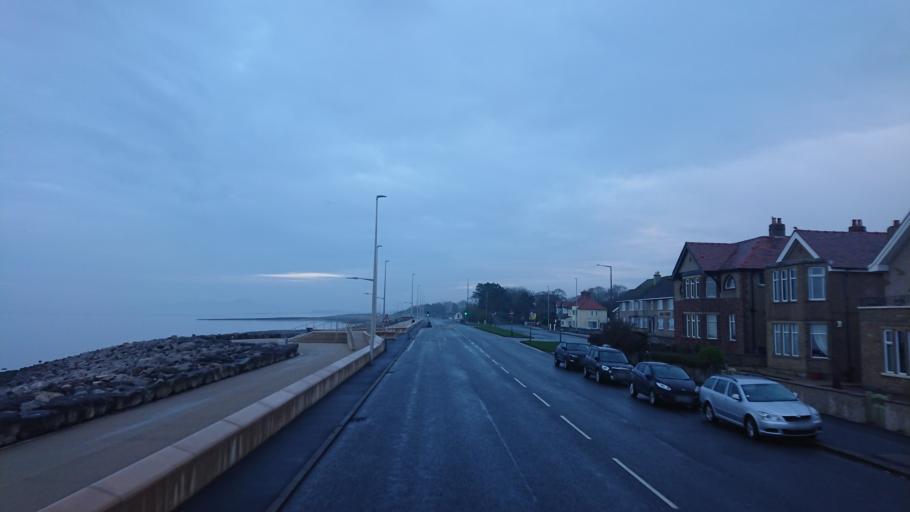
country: GB
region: England
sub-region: Lancashire
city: Morecambe
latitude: 54.0800
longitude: -2.8385
